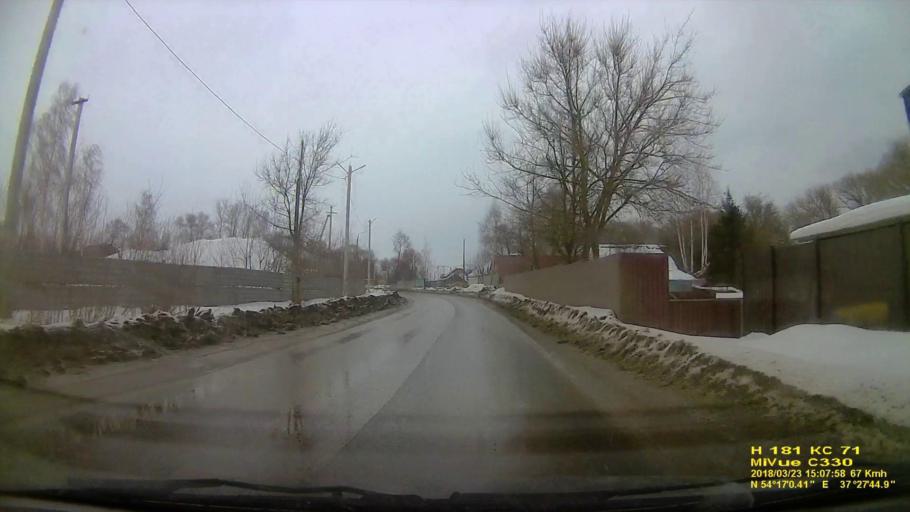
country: RU
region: Tula
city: Leninskiy
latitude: 54.2834
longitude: 37.4625
